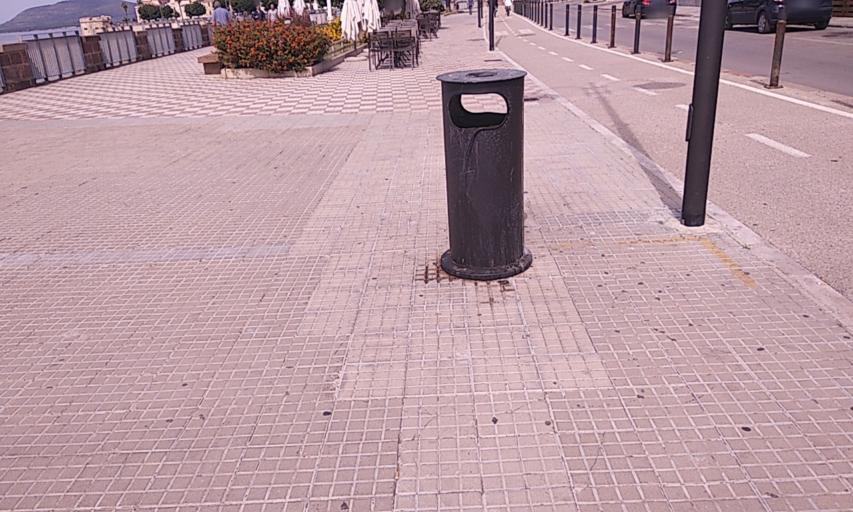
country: IT
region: Sardinia
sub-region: Provincia di Sassari
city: Alghero
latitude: 40.5540
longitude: 8.3159
